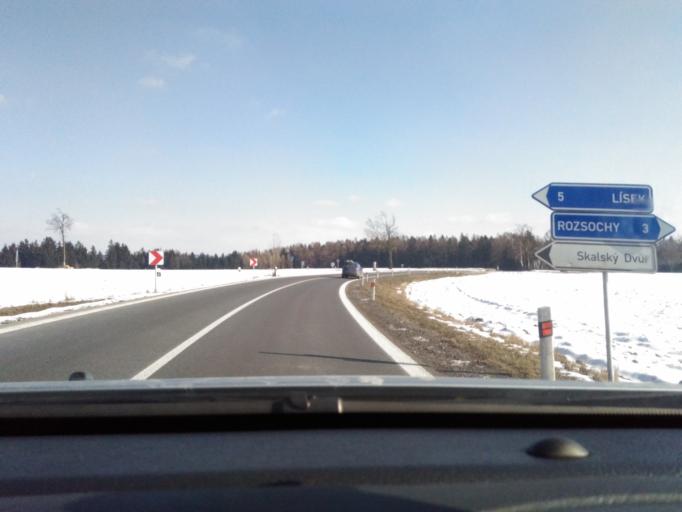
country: CZ
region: Vysocina
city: Bystrice nad Pernstejnem
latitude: 49.5451
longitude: 16.1891
